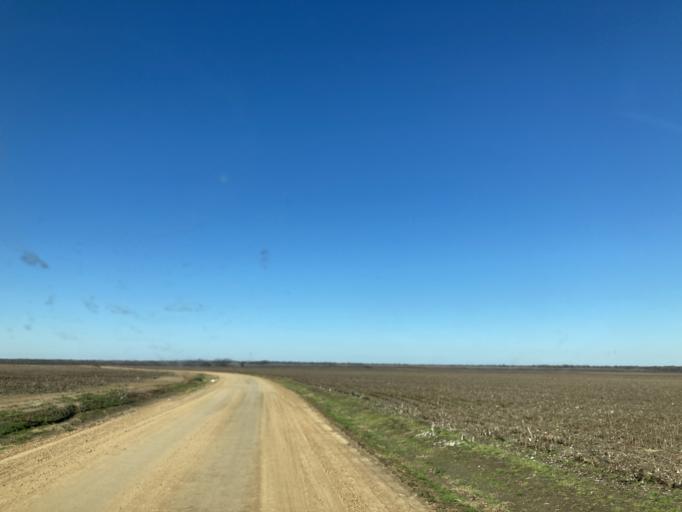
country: US
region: Mississippi
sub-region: Sharkey County
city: Rolling Fork
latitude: 32.8221
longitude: -90.7298
